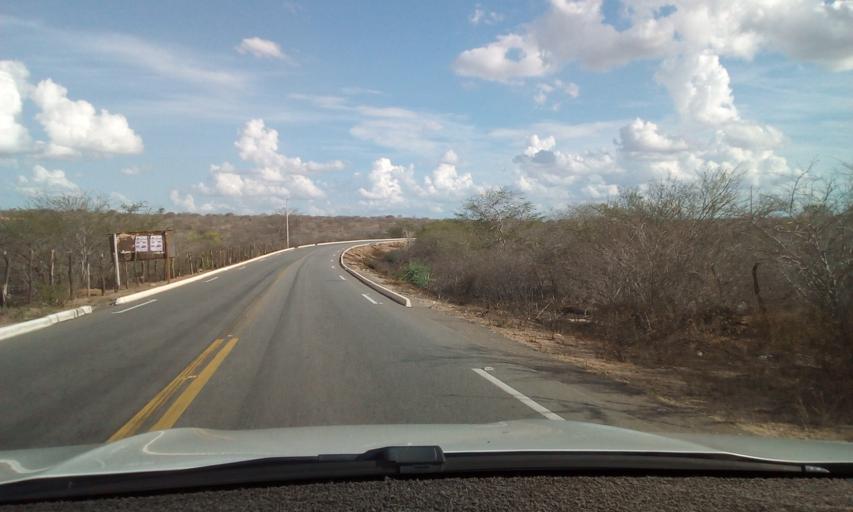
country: BR
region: Paraiba
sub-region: Soledade
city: Soledade
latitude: -6.8975
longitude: -36.3931
